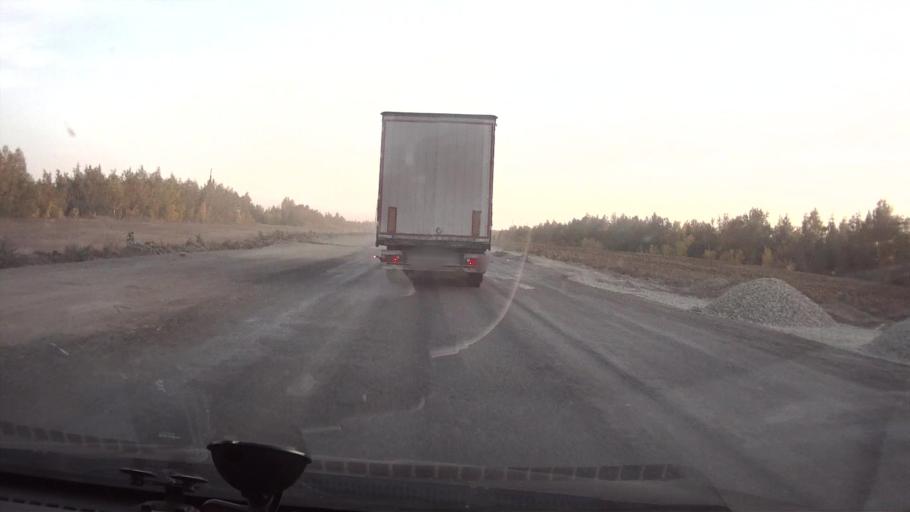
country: RU
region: Saratov
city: Kamenskiy
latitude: 50.9258
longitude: 45.5991
